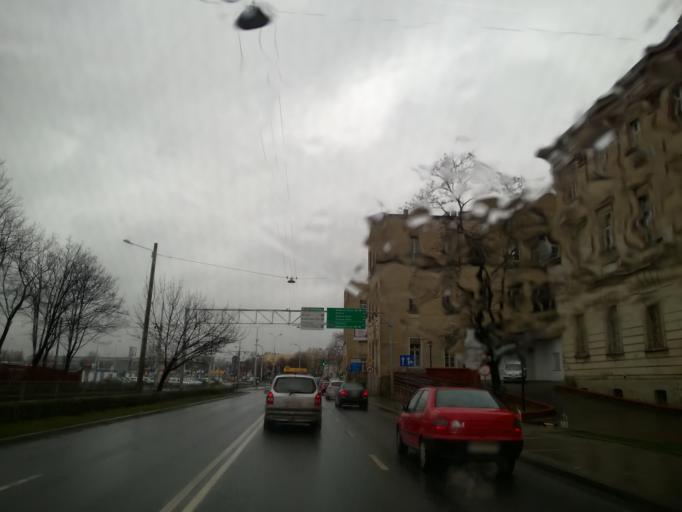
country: PL
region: Lower Silesian Voivodeship
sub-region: Powiat wroclawski
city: Wroclaw
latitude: 51.1033
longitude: 17.0476
